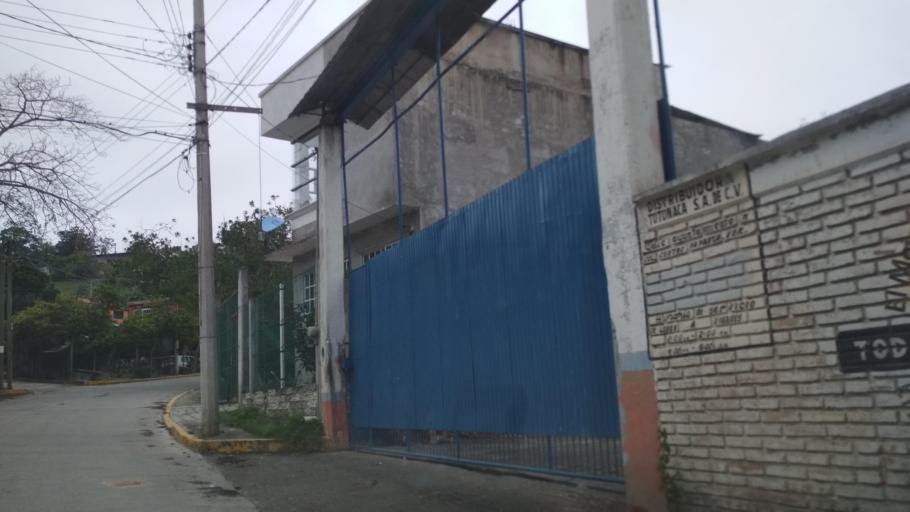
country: MX
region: Veracruz
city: Papantla de Olarte
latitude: 20.4412
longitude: -97.3122
